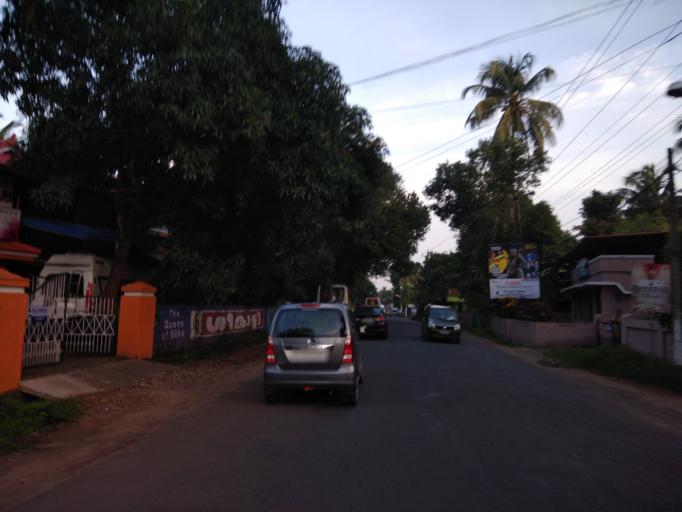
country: IN
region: Kerala
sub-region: Thrissur District
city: Trichur
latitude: 10.5320
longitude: 76.1846
